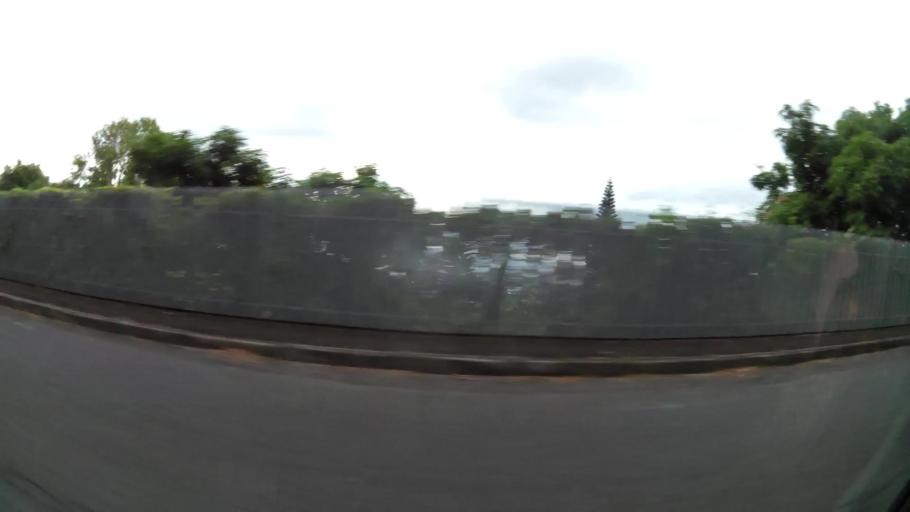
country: RE
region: Reunion
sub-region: Reunion
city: Saint-Denis
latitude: -20.9053
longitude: 55.4673
